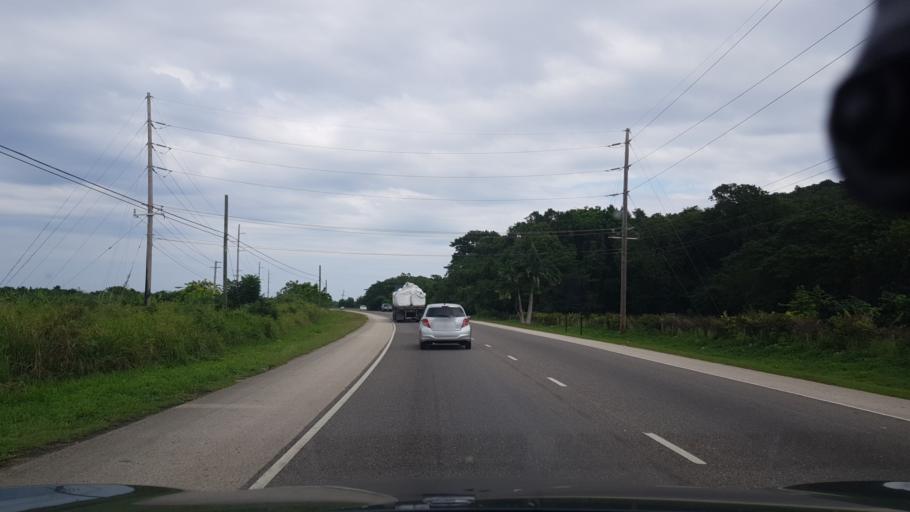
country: JM
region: Trelawny
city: Duncans
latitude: 18.4735
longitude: -77.4903
